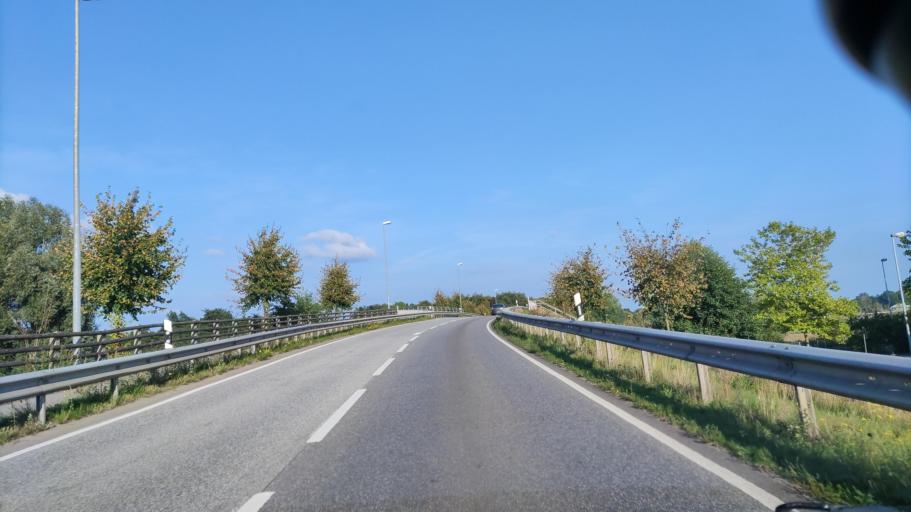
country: DE
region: Schleswig-Holstein
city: Bad Bramstedt
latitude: 53.9165
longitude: 9.8898
